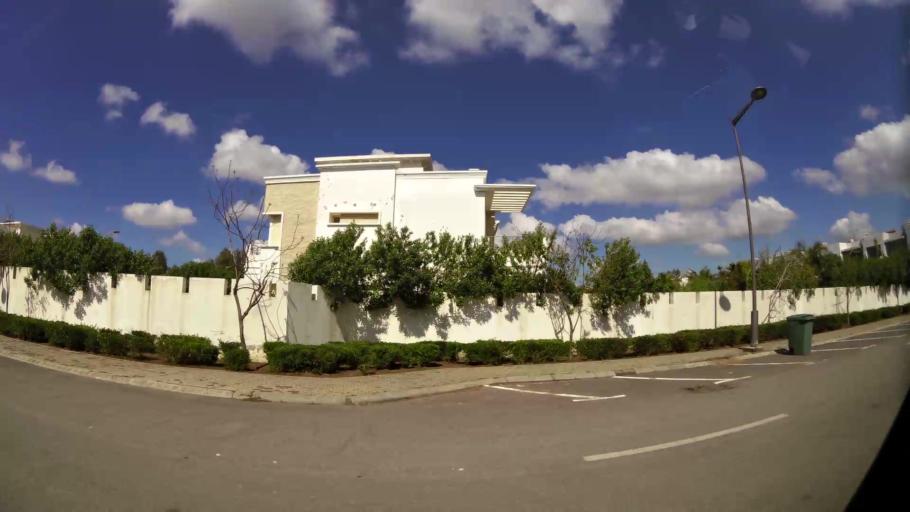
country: MA
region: Grand Casablanca
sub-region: Nouaceur
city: Bouskoura
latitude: 33.4684
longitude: -7.6037
